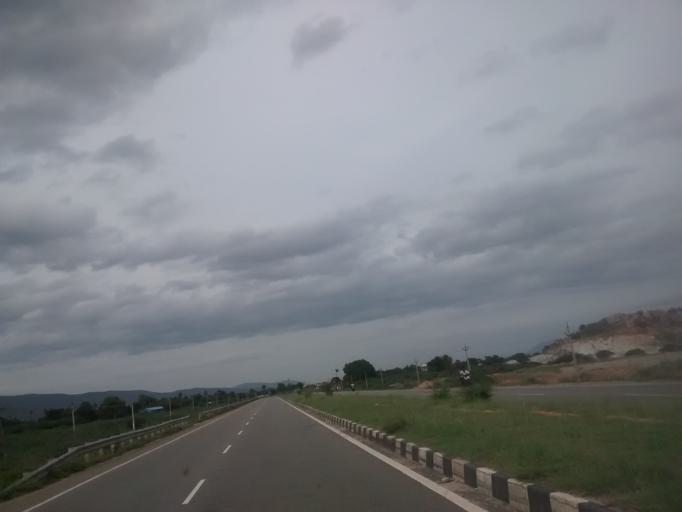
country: IN
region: Andhra Pradesh
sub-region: Chittoor
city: Narasingapuram
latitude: 13.5998
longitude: 79.3605
